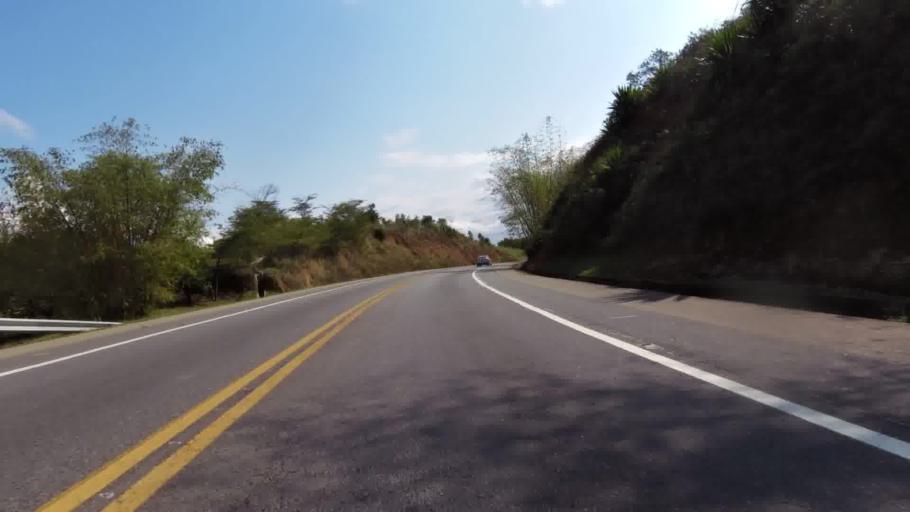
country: BR
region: Rio de Janeiro
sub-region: Macae
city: Macae
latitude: -22.2490
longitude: -41.8124
